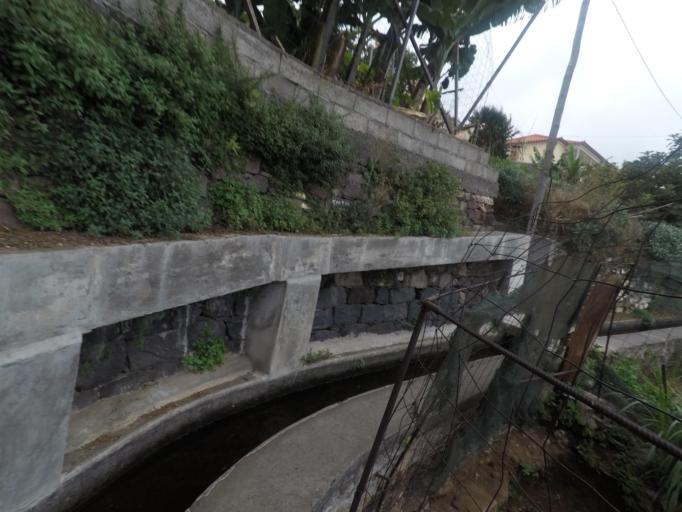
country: PT
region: Madeira
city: Camara de Lobos
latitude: 32.6457
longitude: -16.9526
